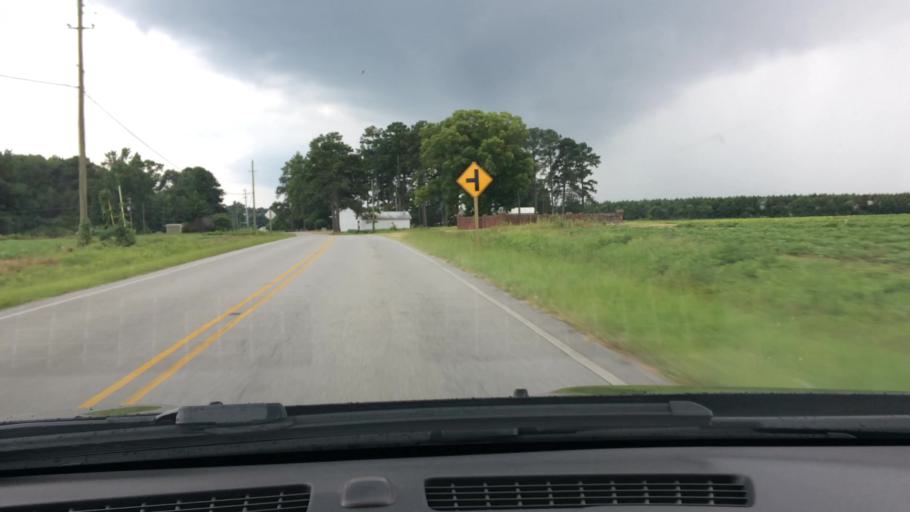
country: US
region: North Carolina
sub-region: Pitt County
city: Ayden
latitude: 35.4834
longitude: -77.3762
